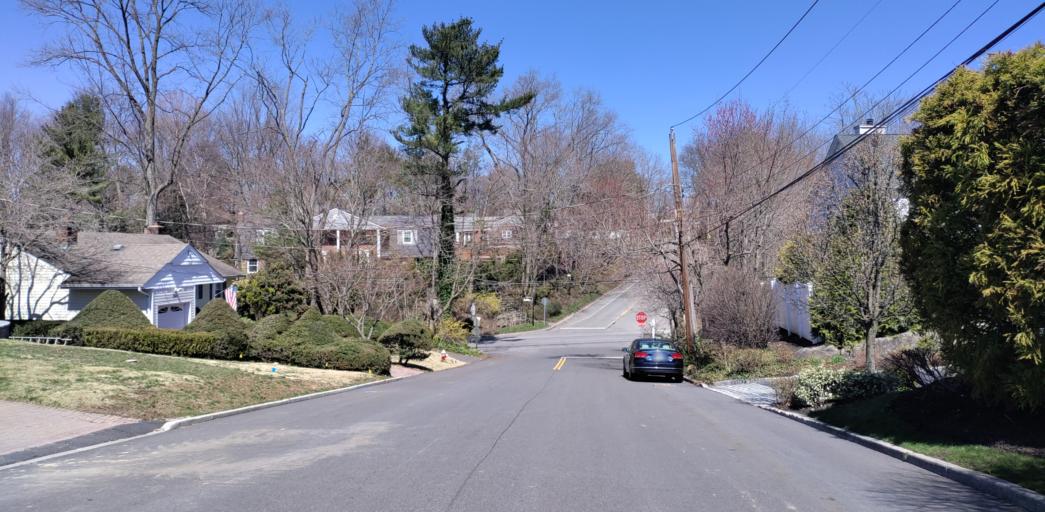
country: US
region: New York
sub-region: Nassau County
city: Glenwood Landing
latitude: 40.8257
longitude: -73.6366
